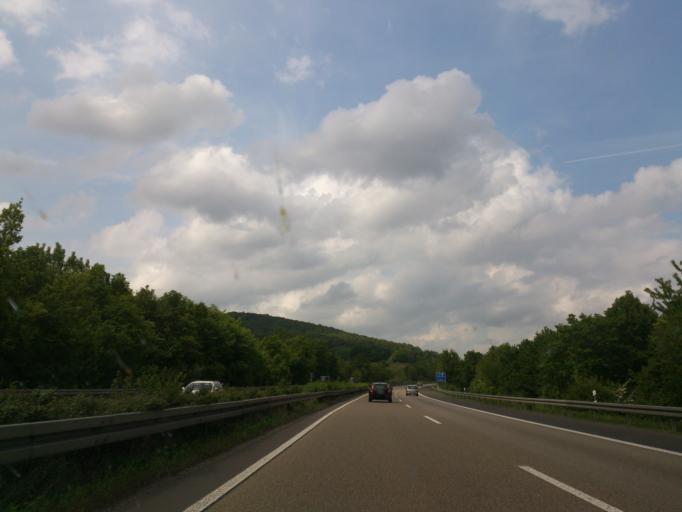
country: DE
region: Hesse
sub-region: Regierungsbezirk Kassel
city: Martinhagen
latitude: 51.3292
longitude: 9.2806
